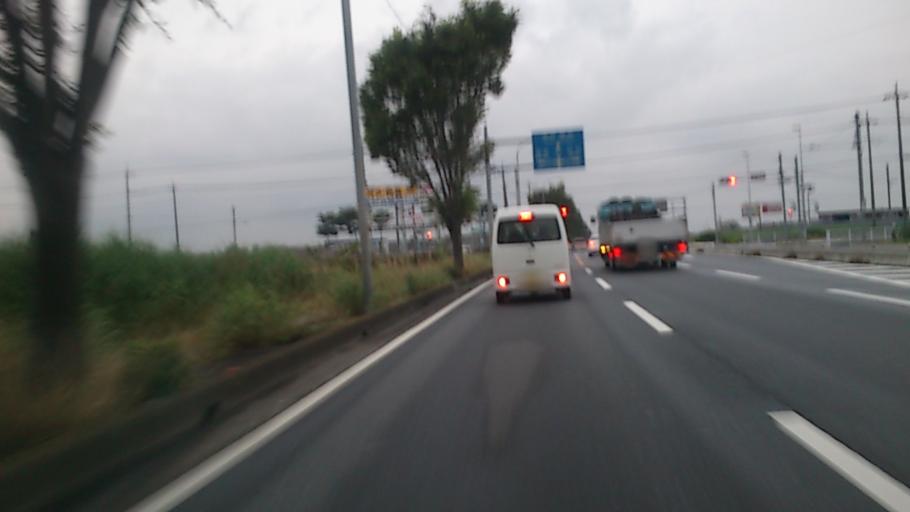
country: JP
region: Saitama
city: Hanyu
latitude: 36.1523
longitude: 139.5092
